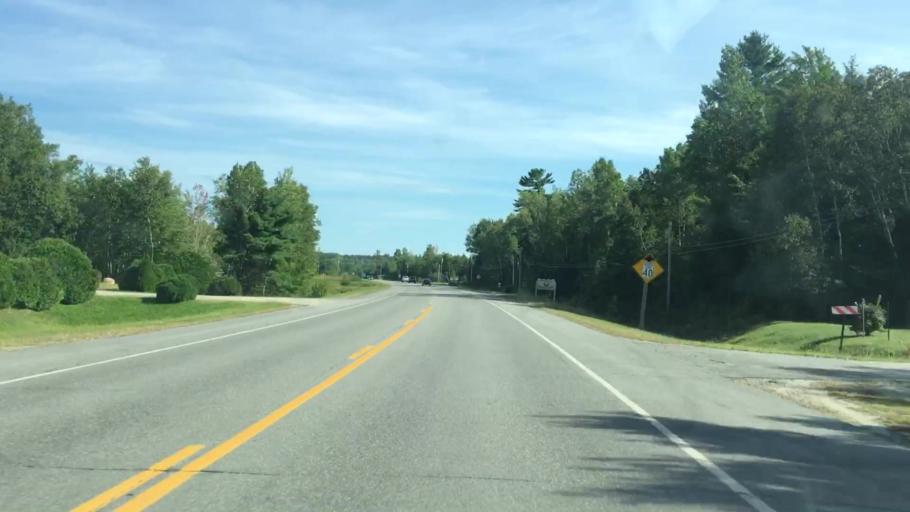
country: US
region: Maine
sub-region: Penobscot County
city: Lincoln
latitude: 45.3600
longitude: -68.5450
